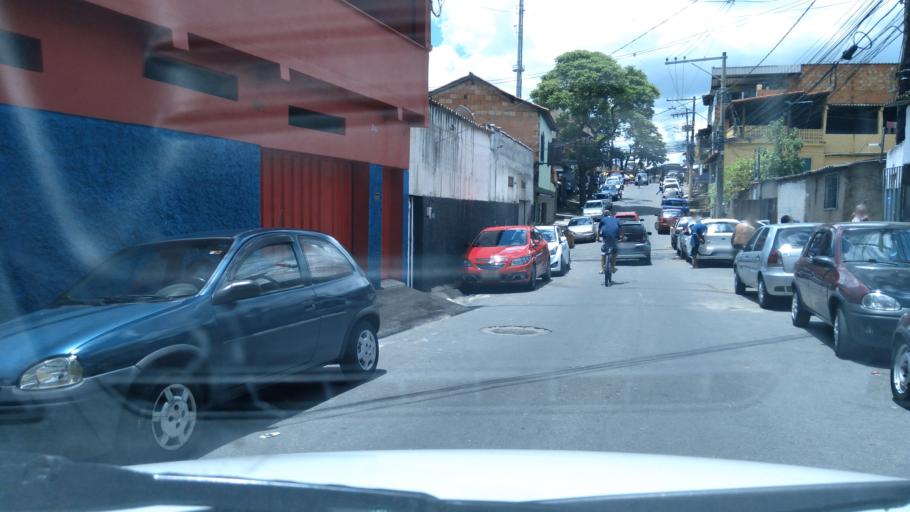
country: BR
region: Minas Gerais
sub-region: Belo Horizonte
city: Belo Horizonte
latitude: -19.9093
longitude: -43.8915
